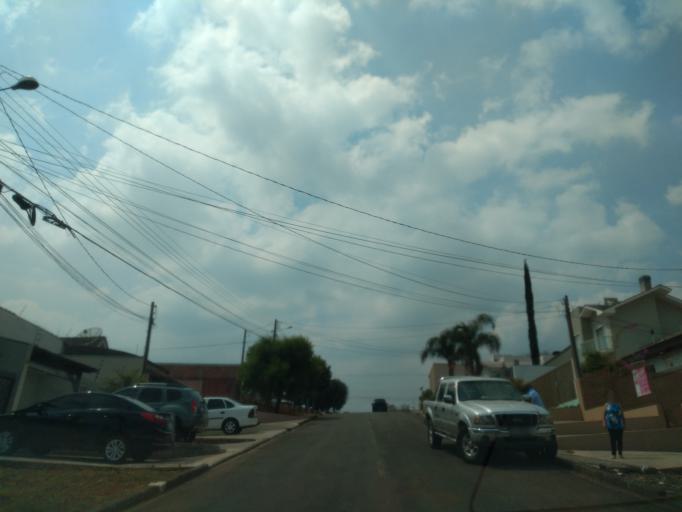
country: BR
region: Parana
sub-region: Guarapuava
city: Guarapuava
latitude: -25.3894
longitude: -51.4824
